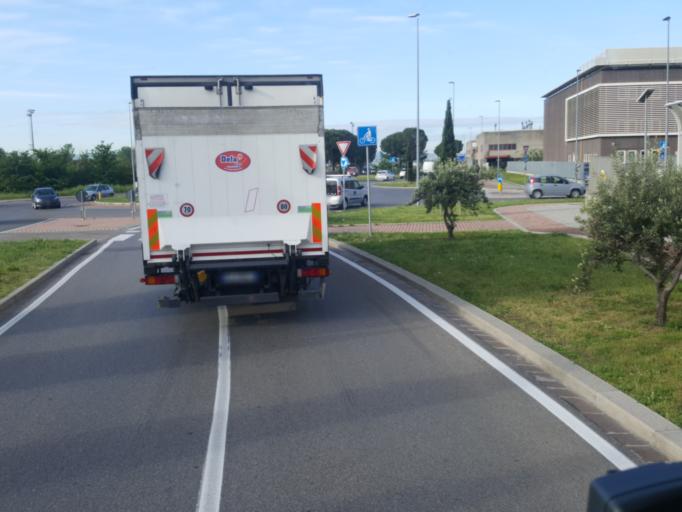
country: IT
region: Tuscany
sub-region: Province of Florence
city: Calenzano
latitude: 43.8401
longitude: 11.1755
